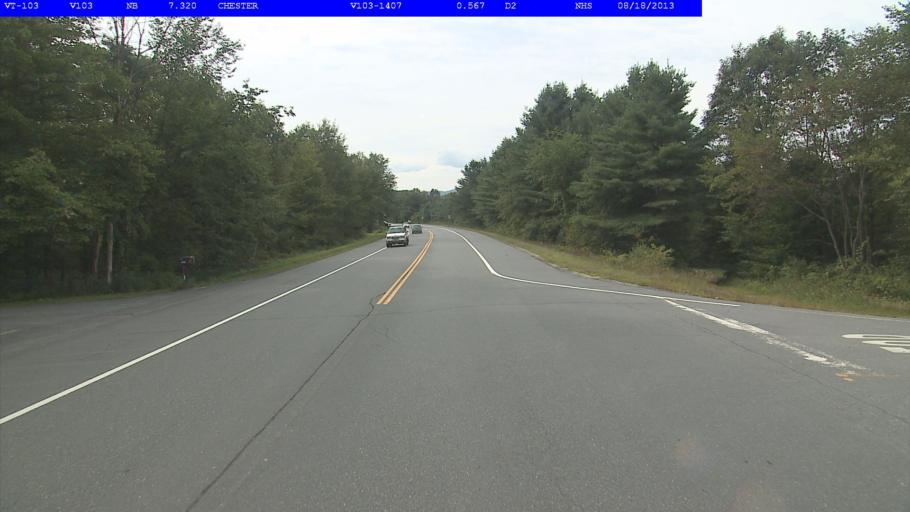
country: US
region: Vermont
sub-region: Windsor County
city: Chester
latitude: 43.2404
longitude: -72.5616
